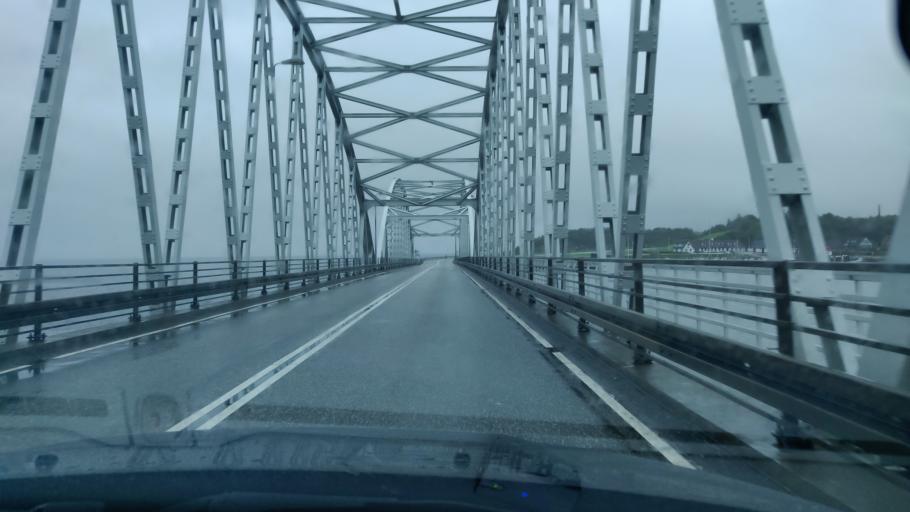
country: DK
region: North Denmark
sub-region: Thisted Kommune
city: Thisted
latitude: 56.8842
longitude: 8.6307
